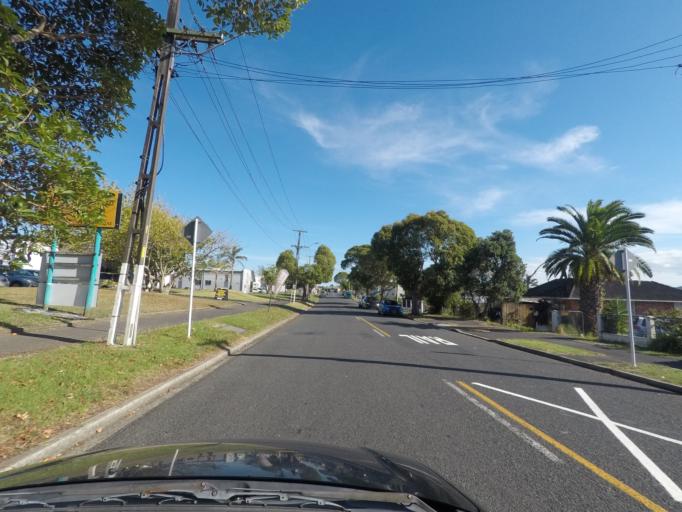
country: NZ
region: Auckland
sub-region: Auckland
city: Waitakere
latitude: -36.9068
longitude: 174.6964
